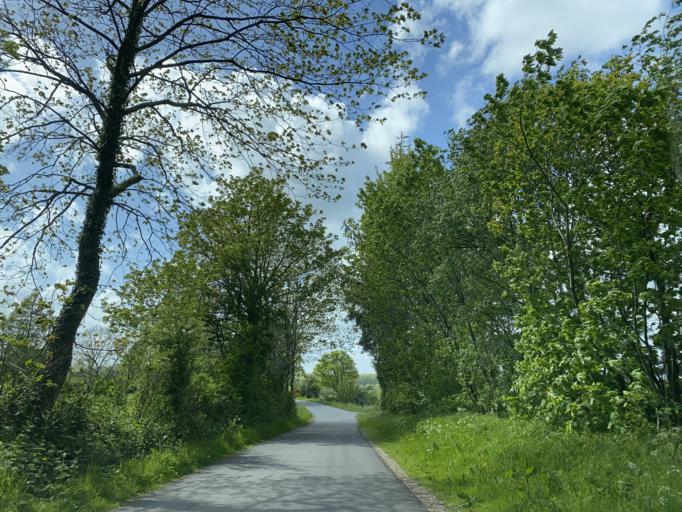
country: DK
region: South Denmark
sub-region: Aabenraa Kommune
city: Aabenraa
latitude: 55.0067
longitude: 9.4566
